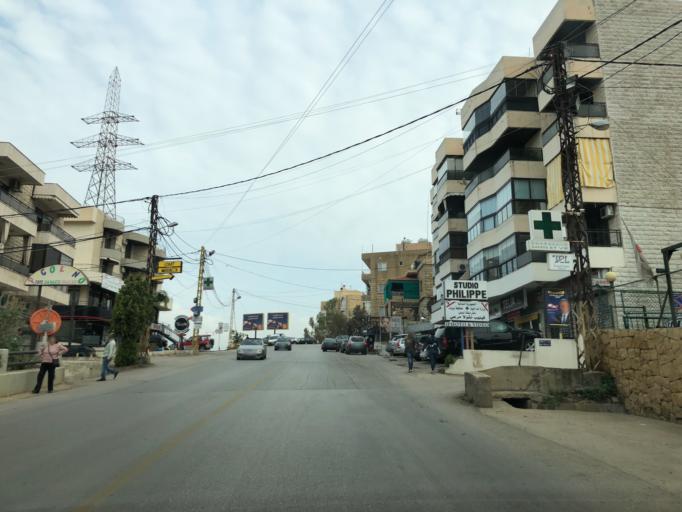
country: LB
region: Mont-Liban
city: Jdaidet el Matn
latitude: 33.8547
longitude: 35.5811
